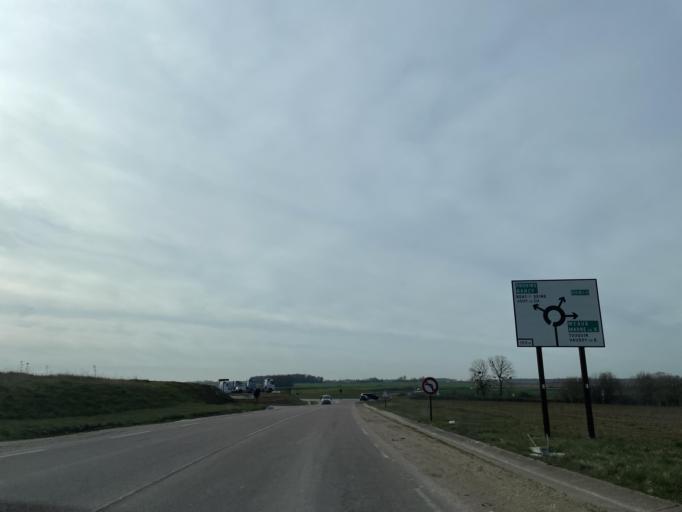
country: FR
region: Ile-de-France
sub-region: Departement de Seine-et-Marne
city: Jouy-le-Chatel
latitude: 48.6886
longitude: 3.1047
